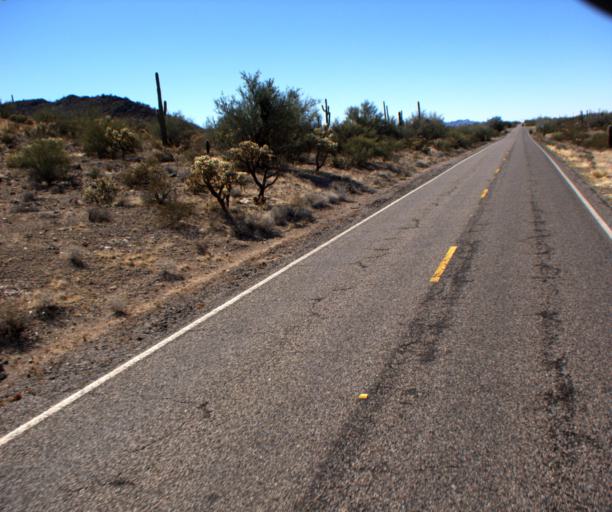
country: US
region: Arizona
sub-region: Pima County
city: Ajo
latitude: 32.2164
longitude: -112.7575
